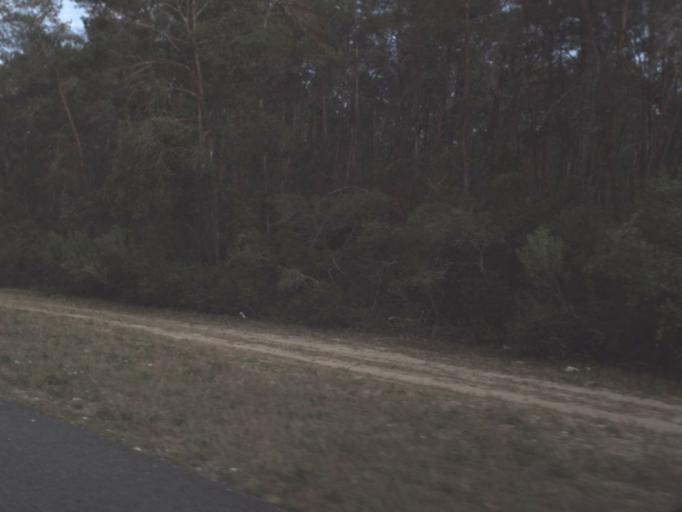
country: US
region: Florida
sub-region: Marion County
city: Silver Springs Shores
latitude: 29.1768
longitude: -81.8017
